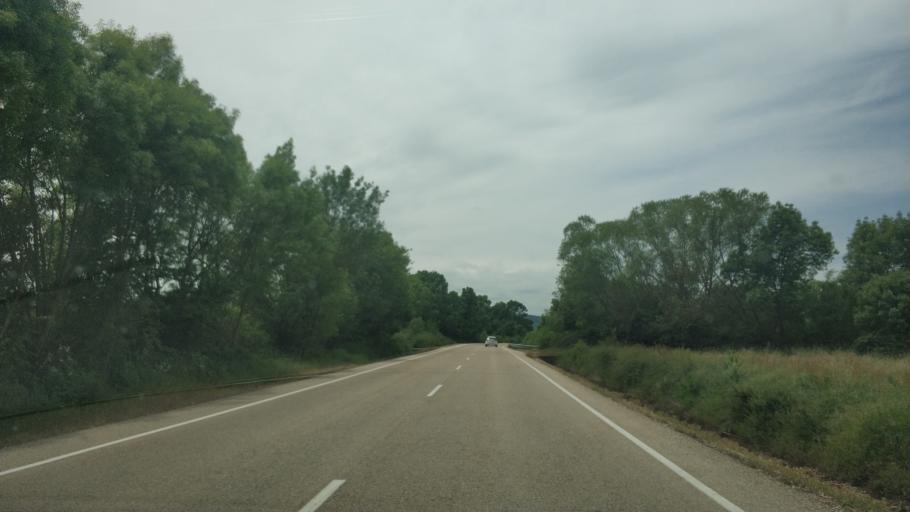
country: ES
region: Castille and Leon
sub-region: Provincia de Soria
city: Sotillo del Rincon
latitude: 41.9037
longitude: -2.6500
